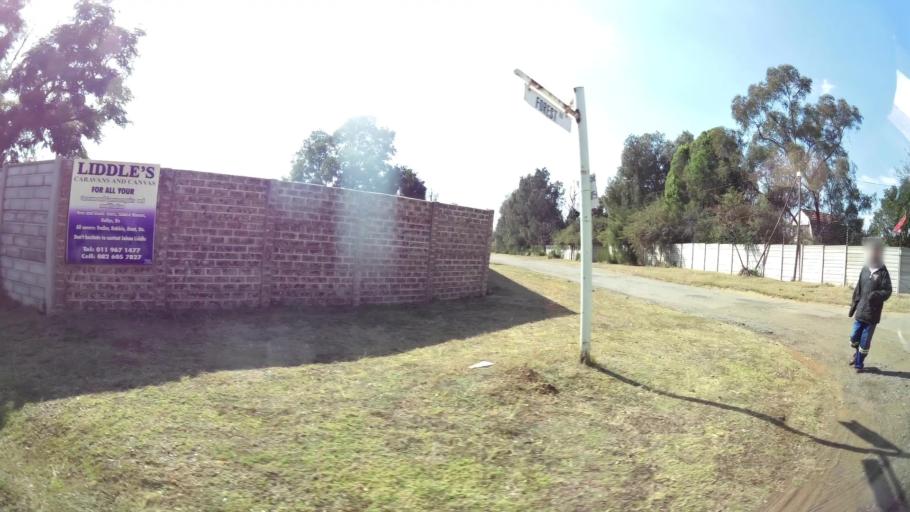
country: ZA
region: Gauteng
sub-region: Ekurhuleni Metropolitan Municipality
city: Benoni
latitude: -26.0921
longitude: 28.3318
